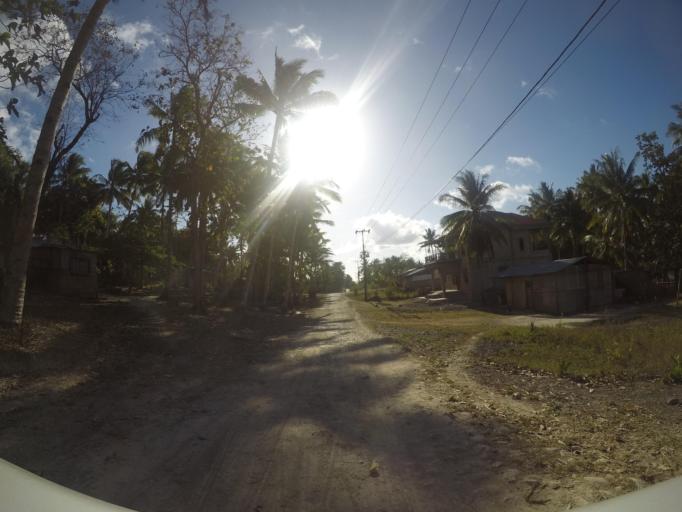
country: TL
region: Lautem
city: Lospalos
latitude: -8.4476
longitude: 126.8793
